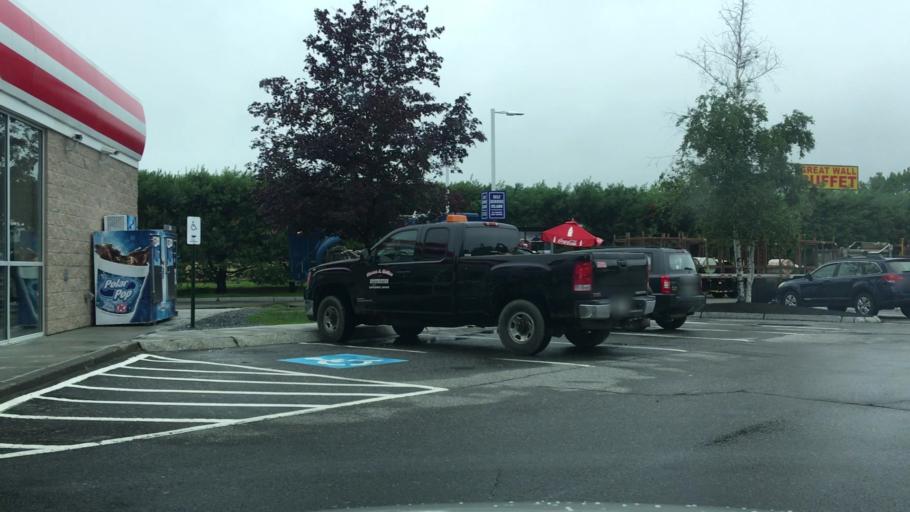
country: US
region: Maine
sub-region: Kennebec County
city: Augusta
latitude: 44.3490
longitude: -69.7967
